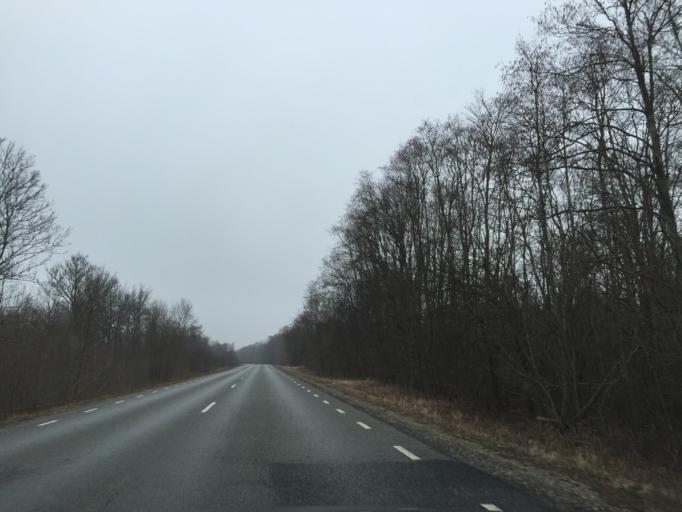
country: EE
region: Laeaene
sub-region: Lihula vald
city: Lihula
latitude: 58.5855
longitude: 23.7197
